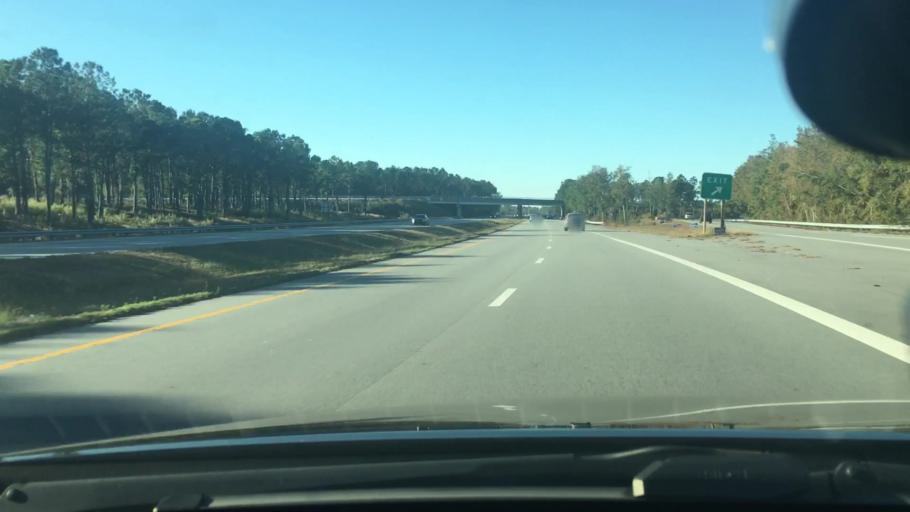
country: US
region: North Carolina
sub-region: Craven County
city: New Bern
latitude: 35.1126
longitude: -77.0101
